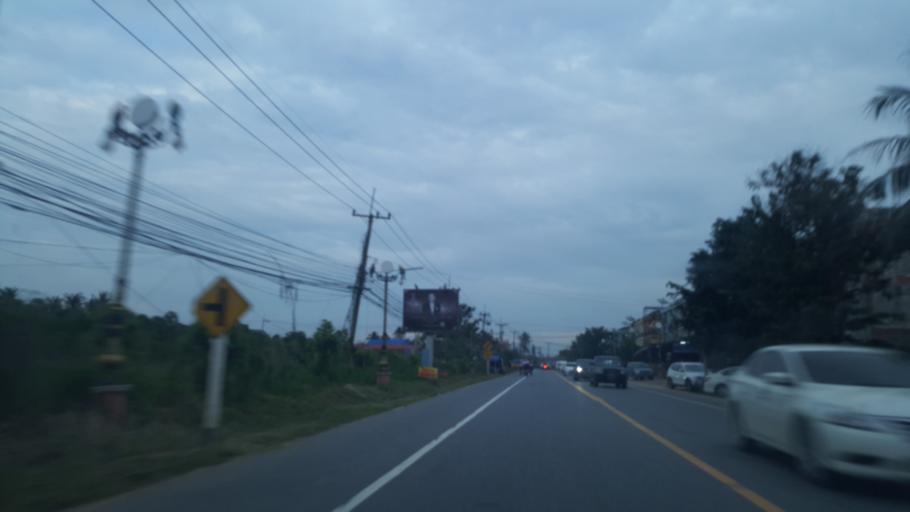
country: TH
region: Chon Buri
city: Ban Talat Bueng
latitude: 12.9531
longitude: 101.0419
